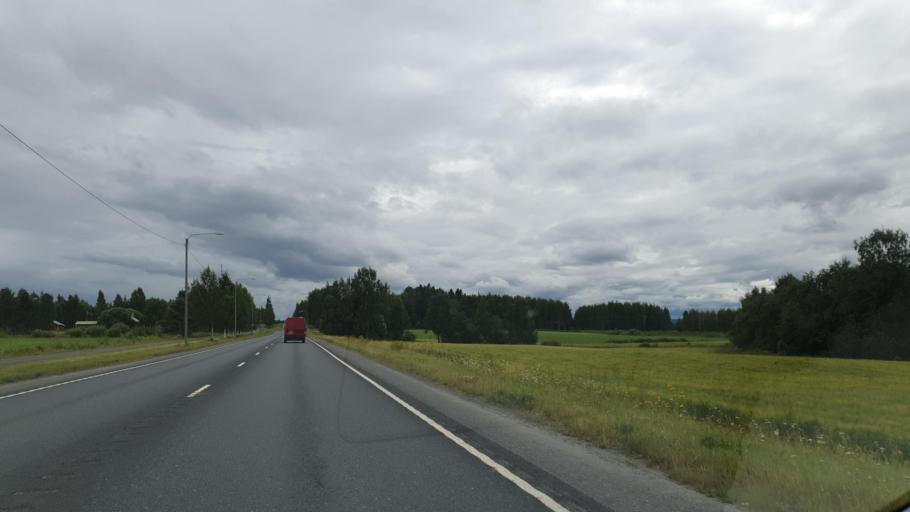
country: FI
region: Northern Savo
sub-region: Ylae-Savo
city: Lapinlahti
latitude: 63.4370
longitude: 27.3259
